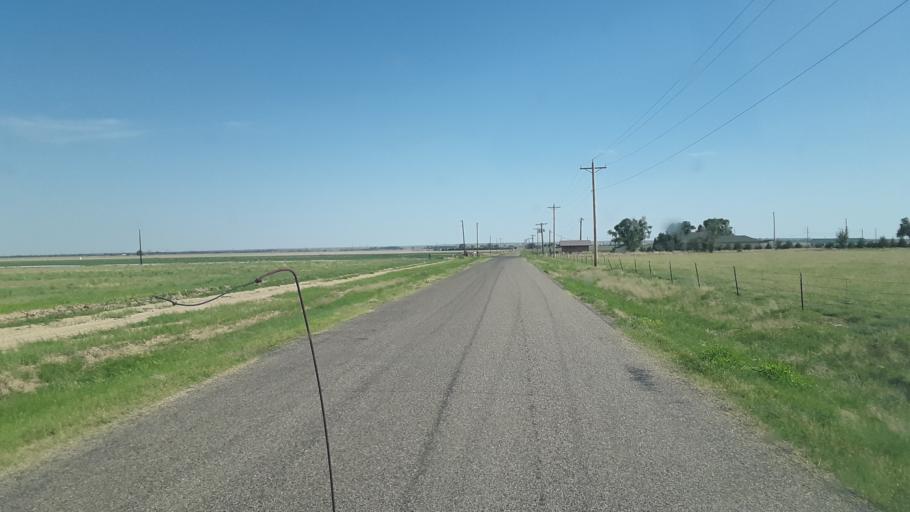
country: US
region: Colorado
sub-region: Otero County
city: Fowler
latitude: 38.1649
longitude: -103.9314
